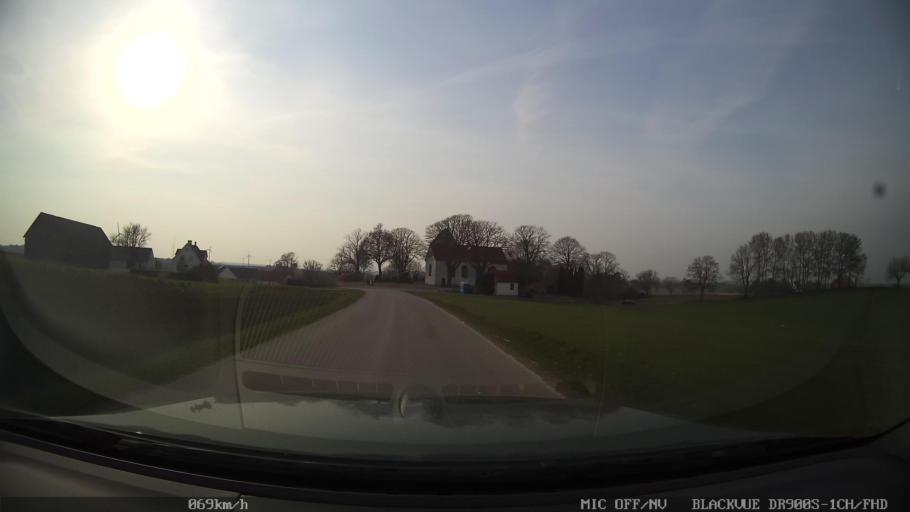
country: SE
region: Skane
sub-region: Ystads Kommun
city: Ystad
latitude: 55.4700
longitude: 13.8033
